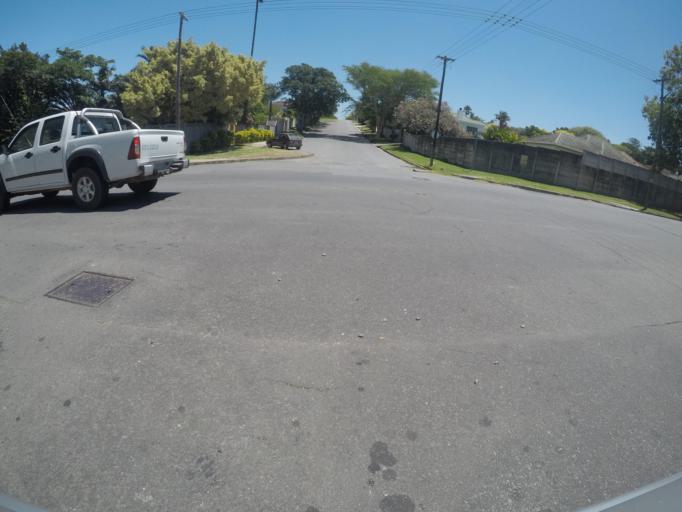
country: ZA
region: Eastern Cape
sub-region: Buffalo City Metropolitan Municipality
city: East London
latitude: -32.9876
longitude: 27.9020
